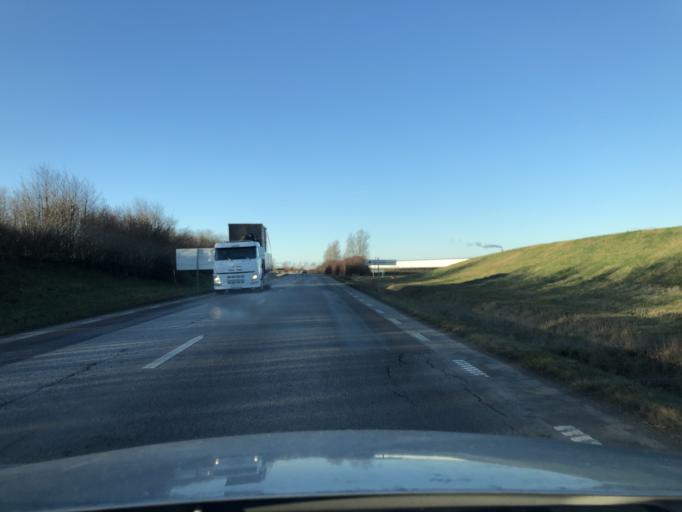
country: SE
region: Skane
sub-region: Trelleborgs Kommun
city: Trelleborg
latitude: 55.3617
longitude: 13.2355
